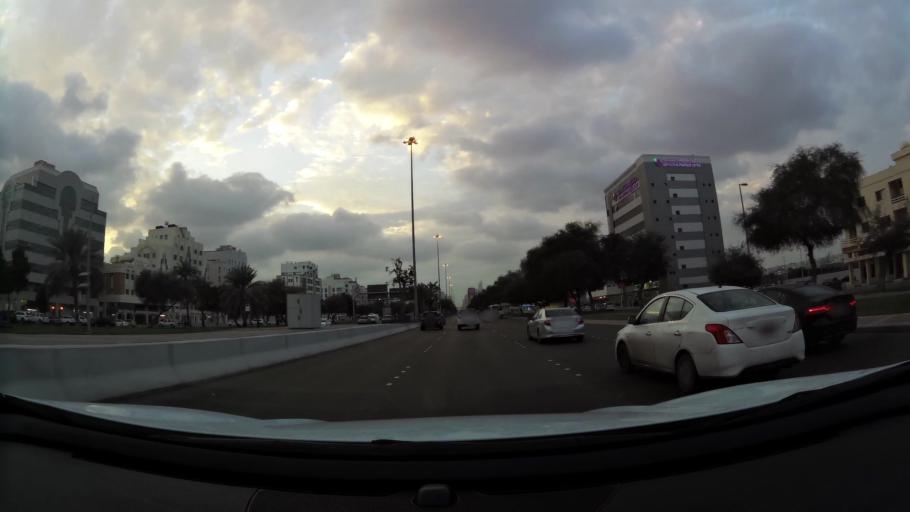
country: AE
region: Abu Dhabi
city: Abu Dhabi
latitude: 24.4507
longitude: 54.3893
